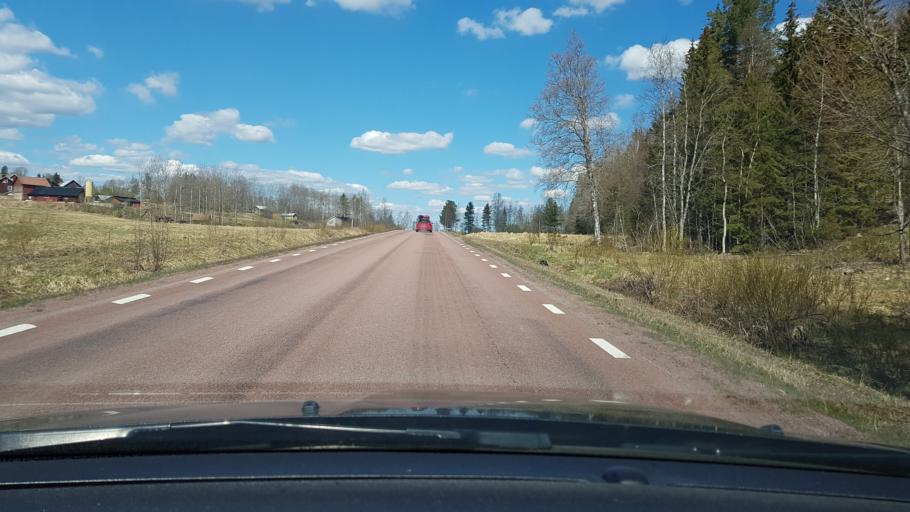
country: SE
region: Dalarna
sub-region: Alvdalens Kommun
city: AElvdalen
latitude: 61.1276
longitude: 13.9662
